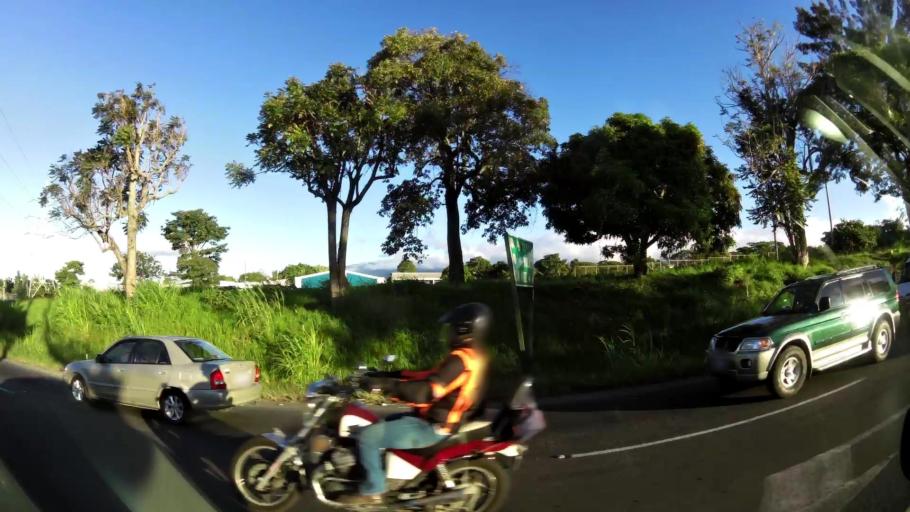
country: CR
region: Heredia
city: Angeles
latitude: 9.9792
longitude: -84.0518
